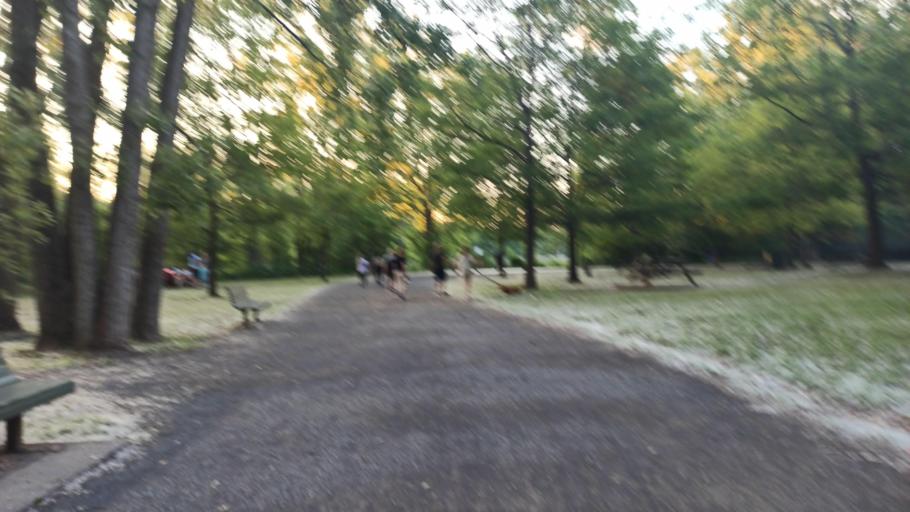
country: CA
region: Quebec
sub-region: Laval
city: Laval
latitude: 45.5781
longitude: -73.6598
